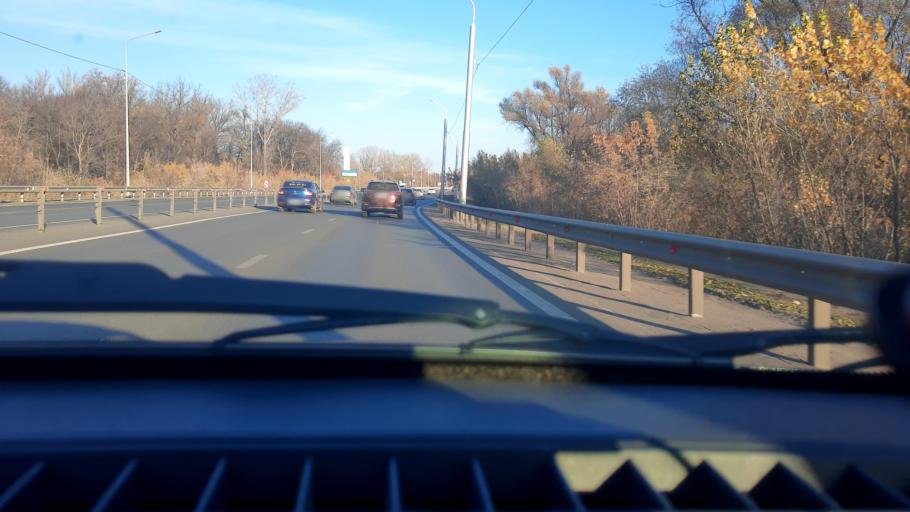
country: RU
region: Bashkortostan
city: Ufa
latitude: 54.6998
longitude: 55.9099
